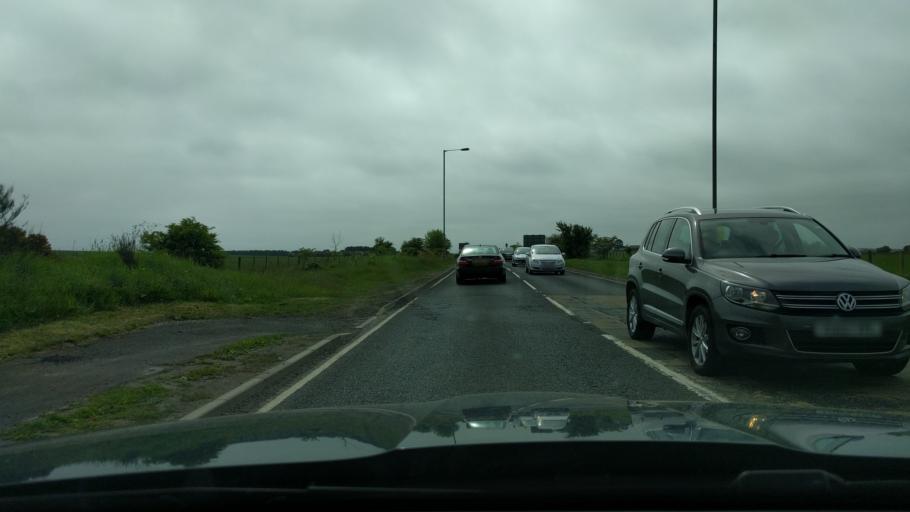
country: GB
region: England
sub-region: Northumberland
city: East Chevington
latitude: 55.2495
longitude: -1.6022
